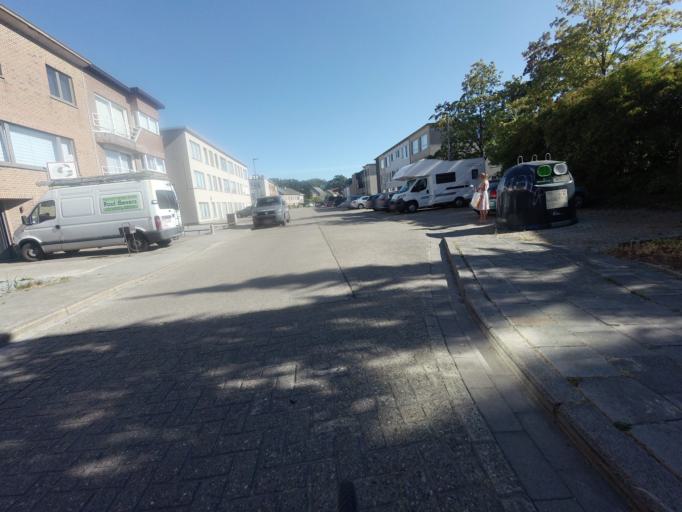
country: BE
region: Flanders
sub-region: Provincie Antwerpen
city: Turnhout
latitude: 51.3301
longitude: 4.9312
